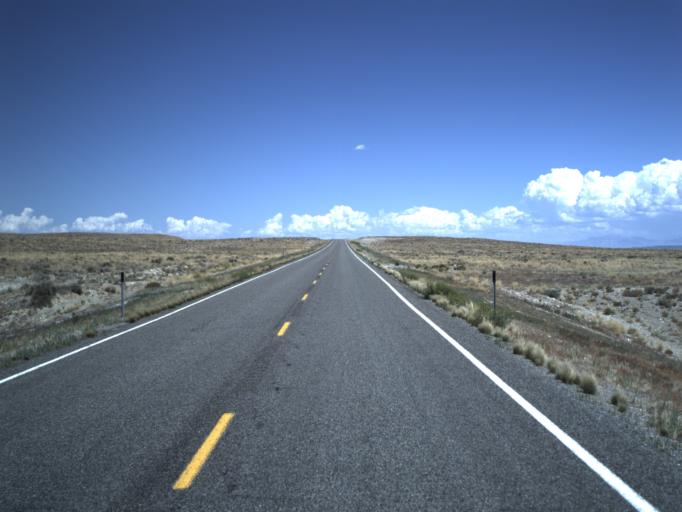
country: US
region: Utah
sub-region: Millard County
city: Delta
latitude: 39.1462
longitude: -113.0761
